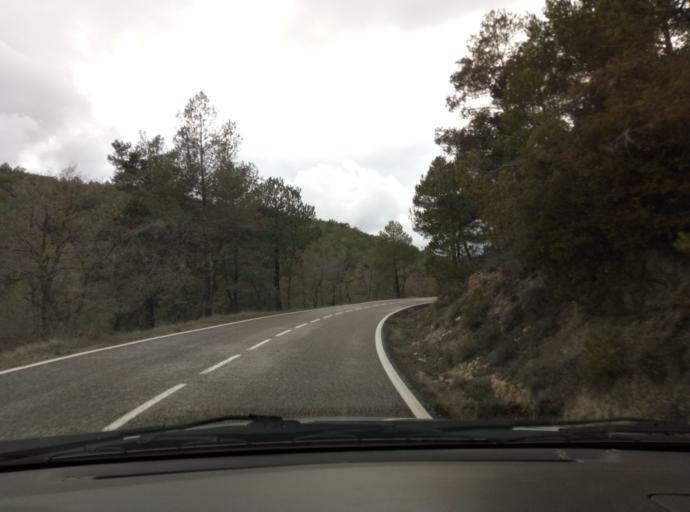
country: ES
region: Catalonia
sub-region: Provincia de Tarragona
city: Santa Coloma de Queralt
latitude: 41.5412
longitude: 1.3408
